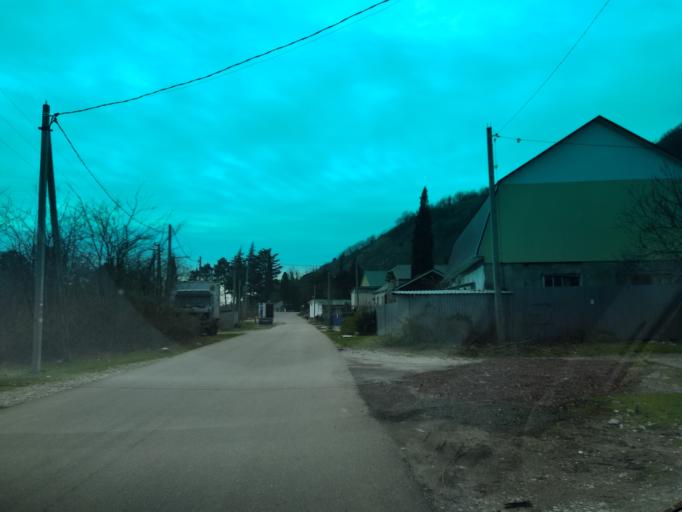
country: RU
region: Krasnodarskiy
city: Shepsi
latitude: 44.0601
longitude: 39.1355
